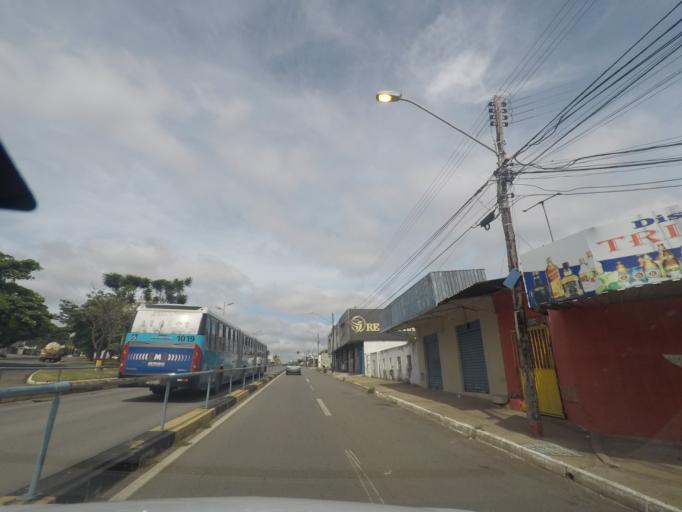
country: BR
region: Goias
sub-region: Goiania
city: Goiania
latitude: -16.6675
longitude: -49.2128
